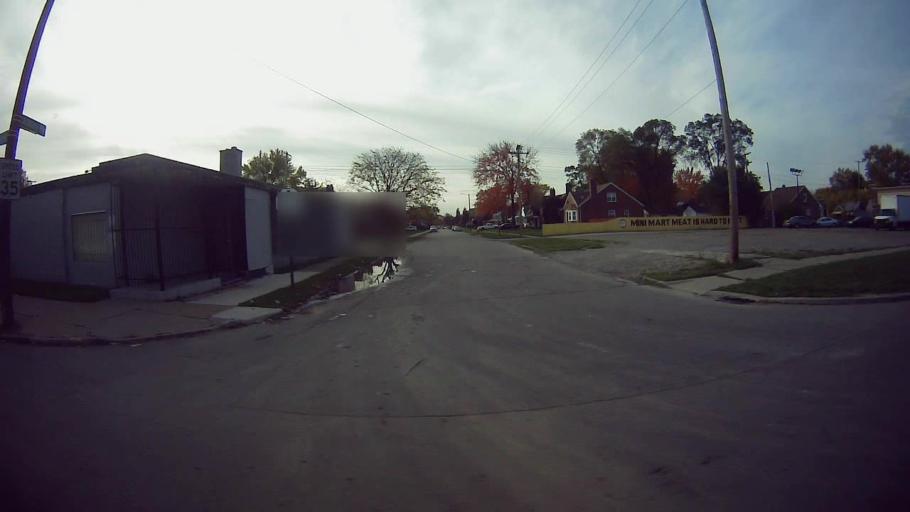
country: US
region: Michigan
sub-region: Oakland County
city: Oak Park
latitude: 42.4158
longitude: -83.2090
